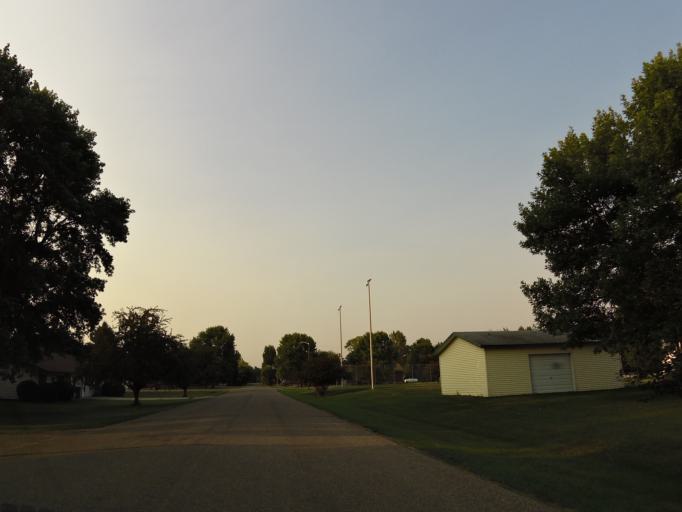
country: US
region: North Dakota
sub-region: Traill County
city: Mayville
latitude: 47.5006
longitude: -97.3725
